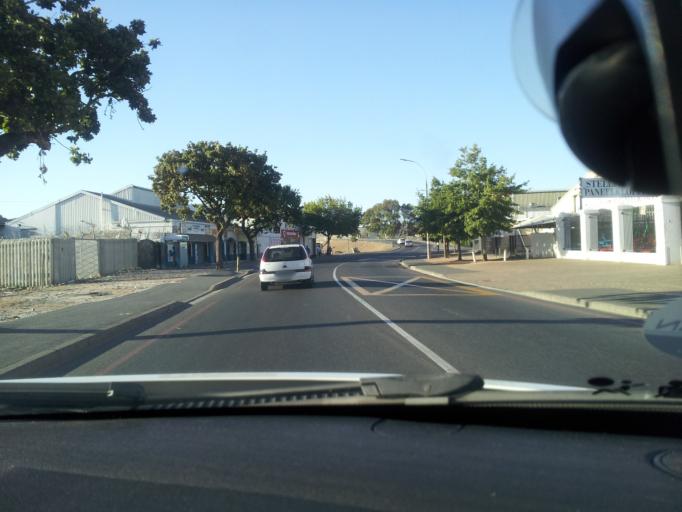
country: ZA
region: Western Cape
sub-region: Cape Winelands District Municipality
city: Stellenbosch
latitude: -33.9227
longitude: 18.8546
